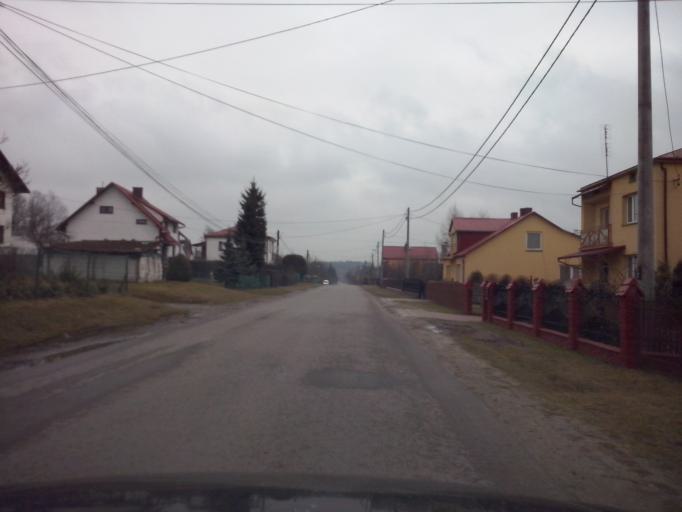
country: PL
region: Subcarpathian Voivodeship
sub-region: Powiat nizanski
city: Bieliny
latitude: 50.4258
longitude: 22.3177
